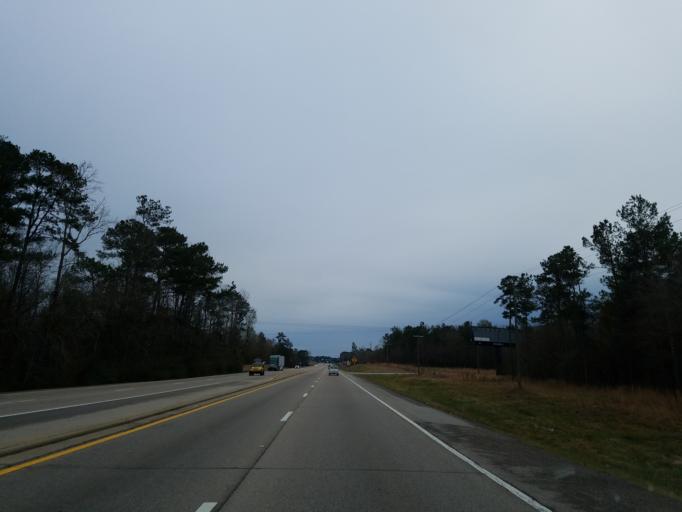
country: US
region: Mississippi
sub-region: Forrest County
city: Hattiesburg
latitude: 31.2886
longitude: -89.3007
